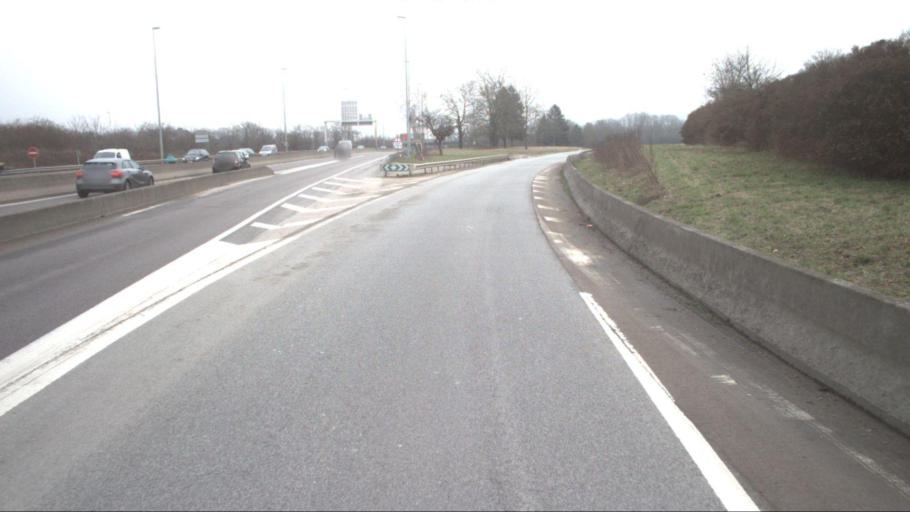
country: FR
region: Ile-de-France
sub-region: Departement des Yvelines
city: Villennes-sur-Seine
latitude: 48.9230
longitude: 1.9989
